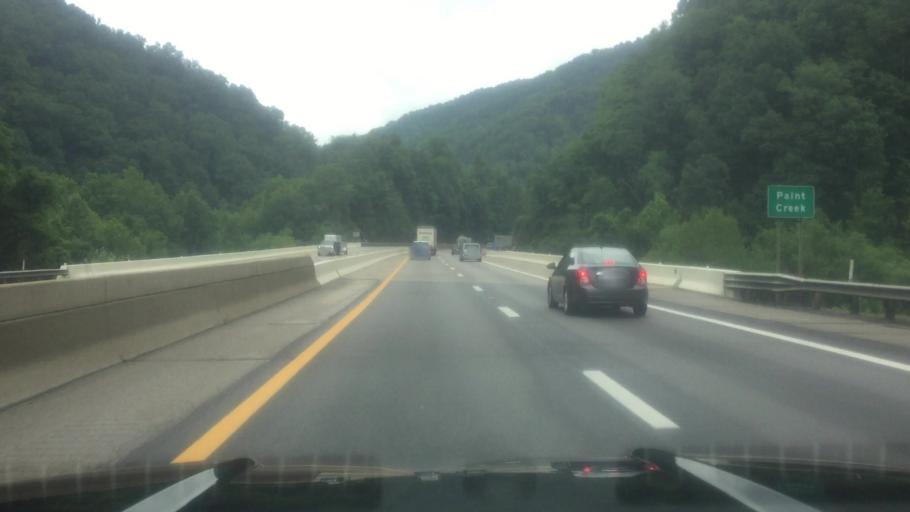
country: US
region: West Virginia
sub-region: Kanawha County
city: Montgomery
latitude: 38.0197
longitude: -81.3540
